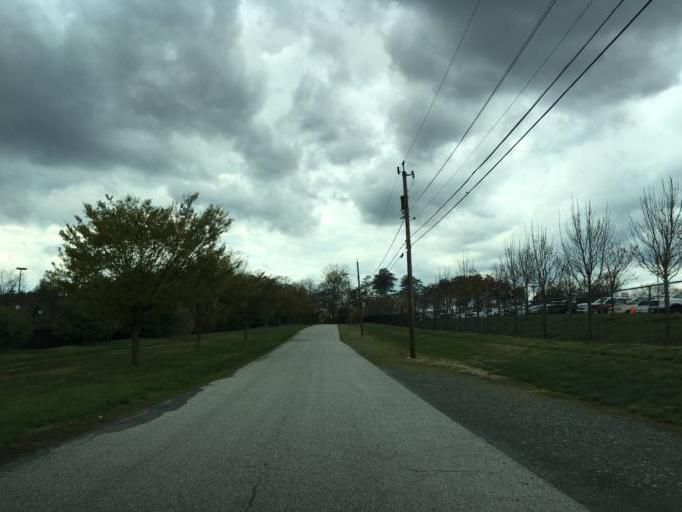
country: US
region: Maryland
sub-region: Howard County
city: Hanover
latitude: 39.1807
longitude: -76.7096
